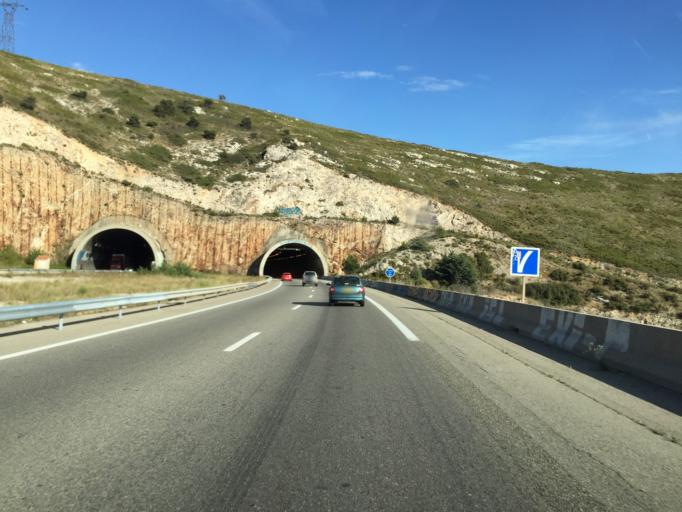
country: FR
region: Provence-Alpes-Cote d'Azur
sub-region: Departement des Bouches-du-Rhone
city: Marseille 16
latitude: 43.3707
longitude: 5.3214
